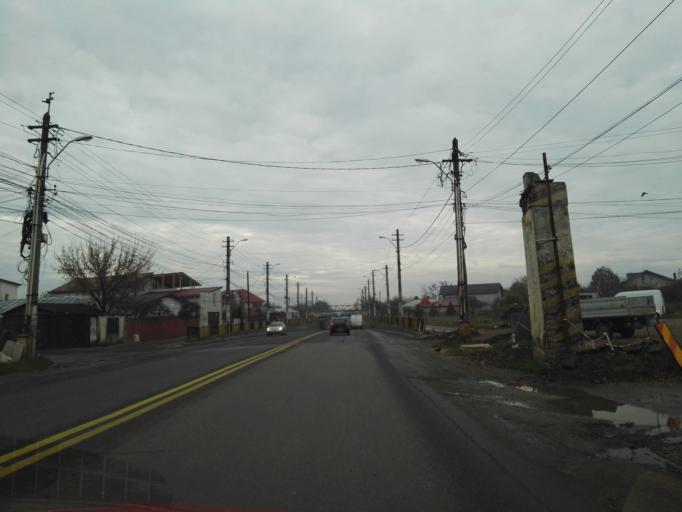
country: RO
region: Ilfov
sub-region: Comuna Jilava
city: Jilava
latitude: 44.3458
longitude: 26.0829
